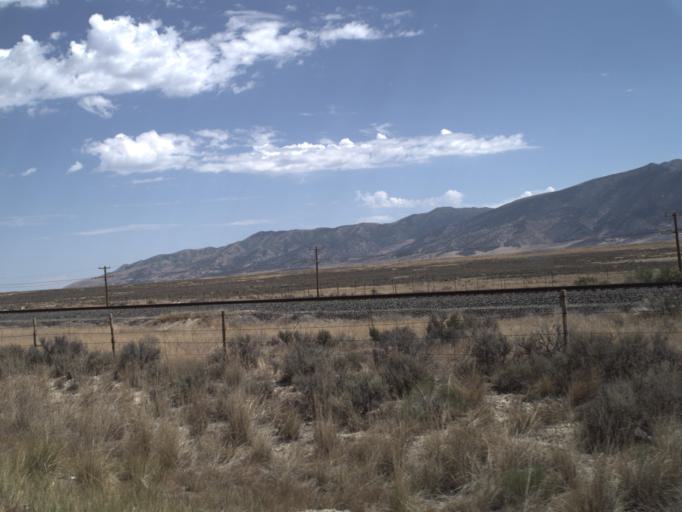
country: US
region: Utah
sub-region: Tooele County
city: Tooele
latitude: 40.3254
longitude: -112.4073
